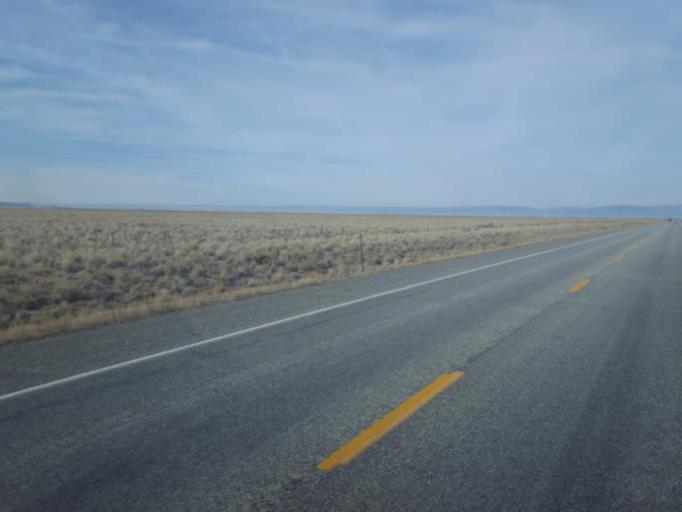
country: US
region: Colorado
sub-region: Alamosa County
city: Alamosa East
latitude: 37.4750
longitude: -105.6165
